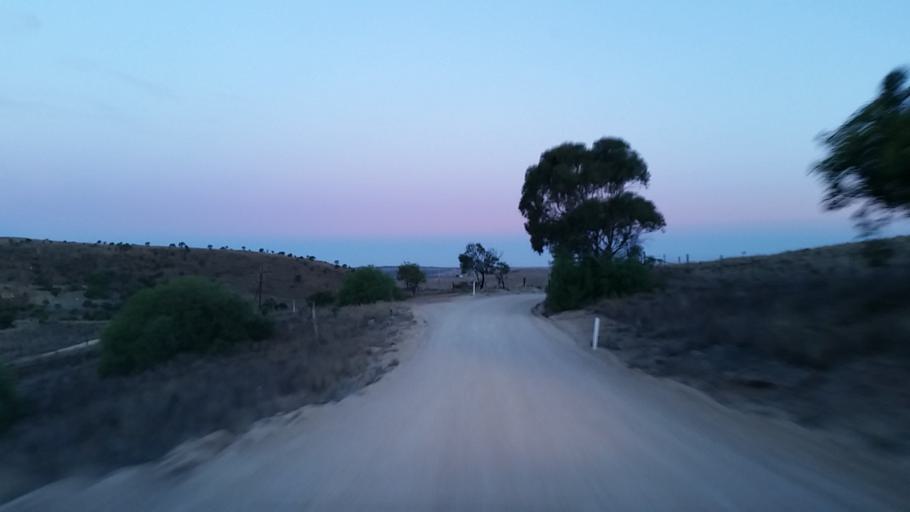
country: AU
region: South Australia
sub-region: Mount Barker
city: Callington
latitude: -35.0985
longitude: 138.9969
